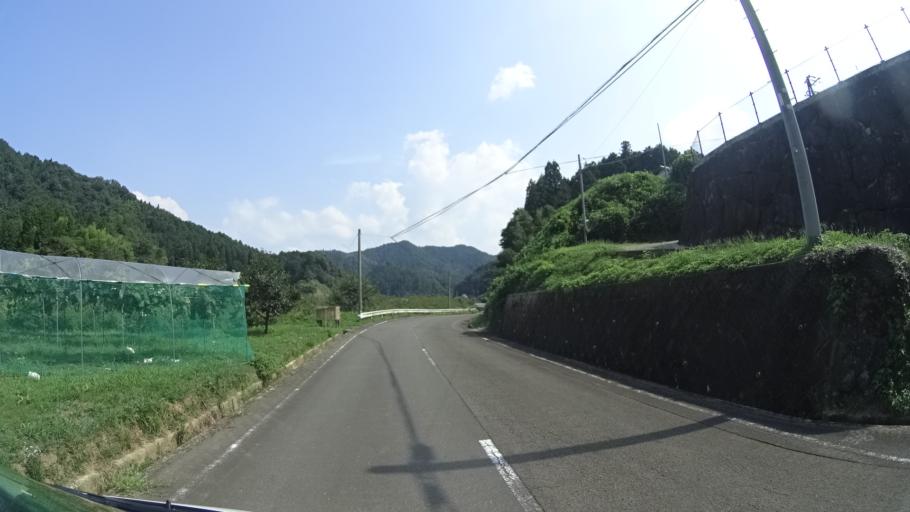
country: JP
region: Kyoto
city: Ayabe
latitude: 35.4081
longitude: 135.1965
